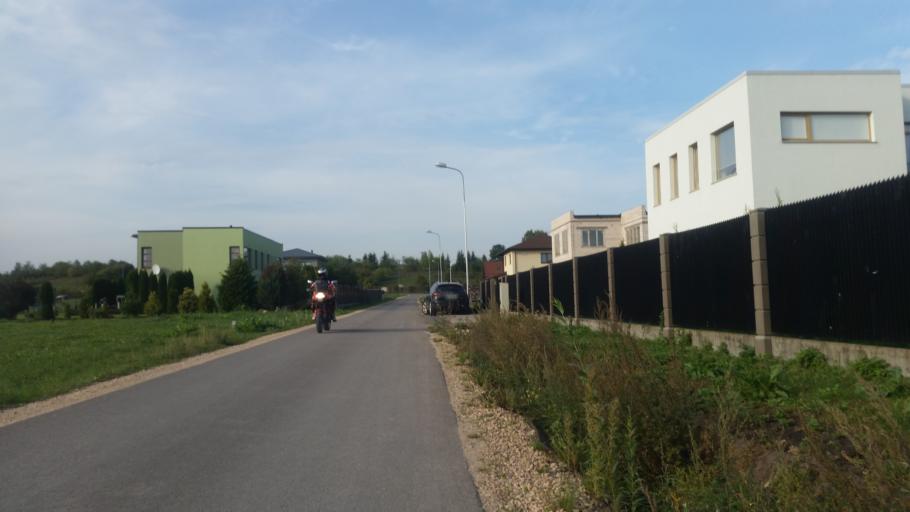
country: LV
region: Ikskile
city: Ikskile
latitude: 56.8175
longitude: 24.5114
